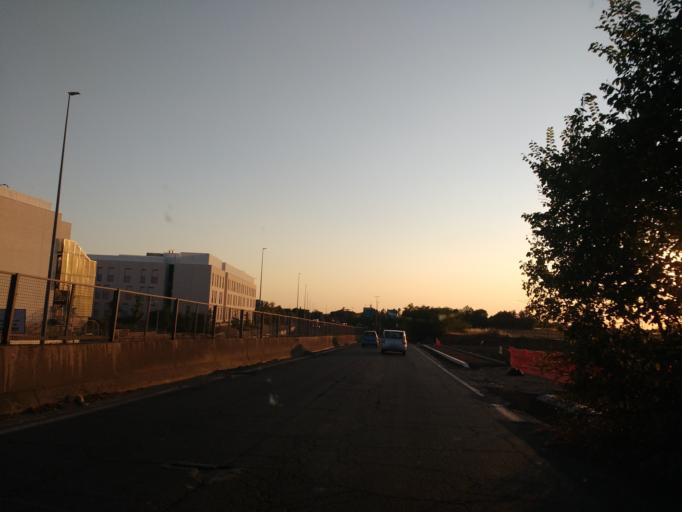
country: IT
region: Latium
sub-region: Citta metropolitana di Roma Capitale
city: Setteville
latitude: 41.9416
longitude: 12.6413
